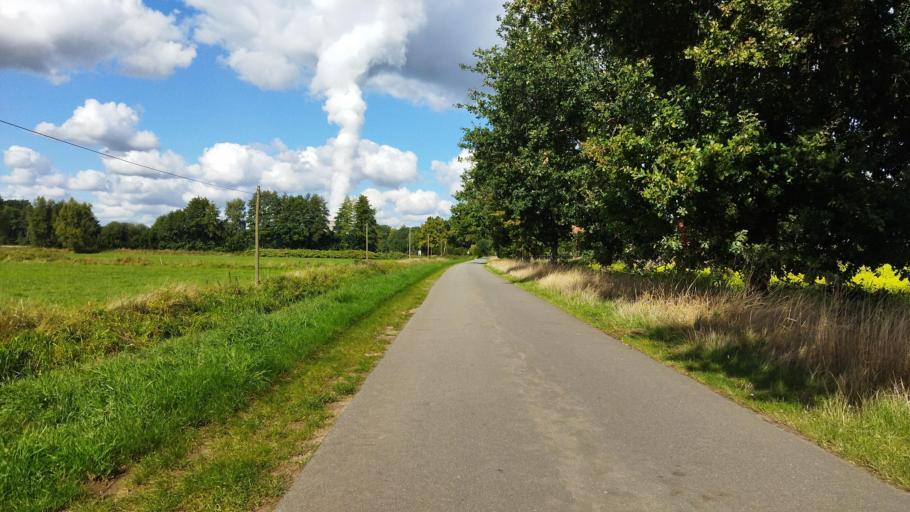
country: DE
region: Lower Saxony
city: Emsburen
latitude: 52.4446
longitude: 7.3381
